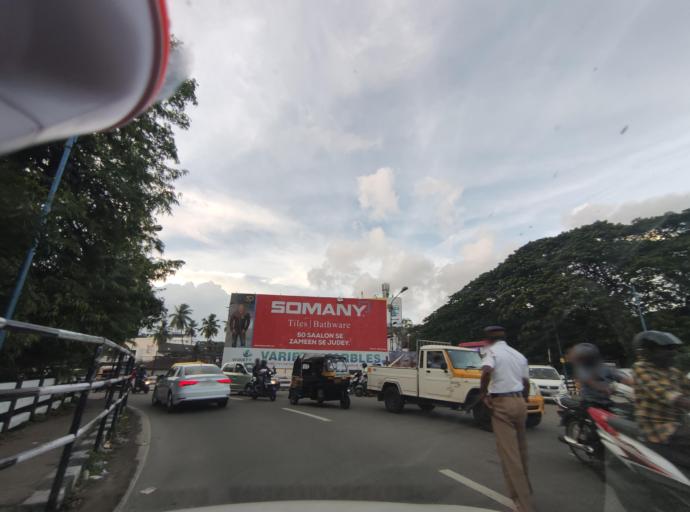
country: IN
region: Kerala
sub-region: Thiruvananthapuram
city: Thiruvananthapuram
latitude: 8.4859
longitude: 76.9549
